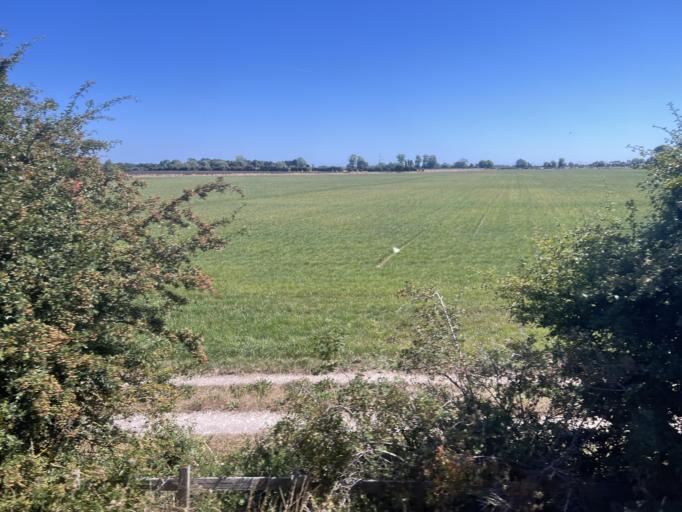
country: GB
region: England
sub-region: Lincolnshire
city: Wainfleet All Saints
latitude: 53.1337
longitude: 0.1909
